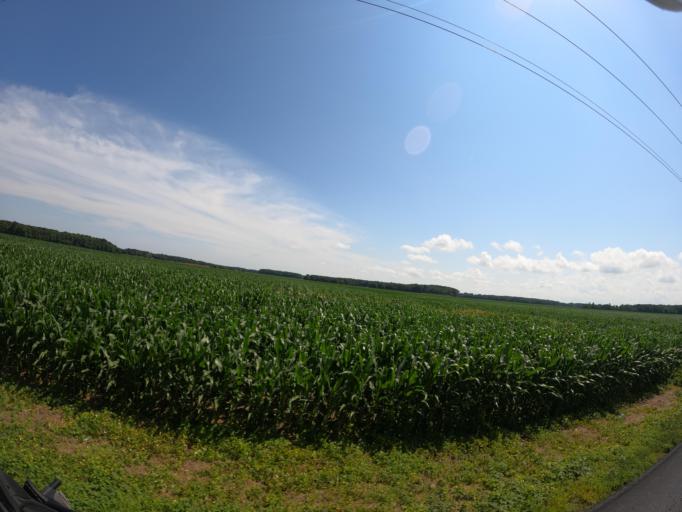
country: US
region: Maryland
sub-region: Worcester County
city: Ocean Pines
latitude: 38.4514
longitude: -75.1610
